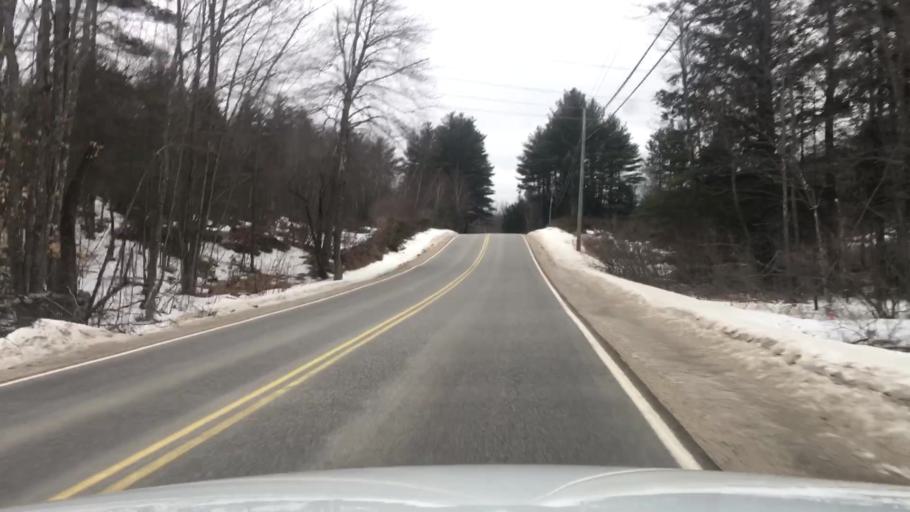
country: US
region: Maine
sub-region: York County
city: Shapleigh
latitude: 43.5107
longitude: -70.8161
